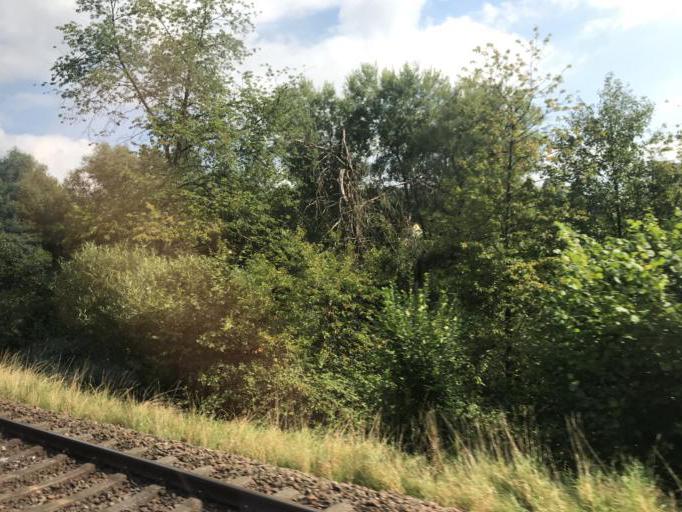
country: DE
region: Saarland
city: Ottweiler
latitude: 49.3942
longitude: 7.1697
